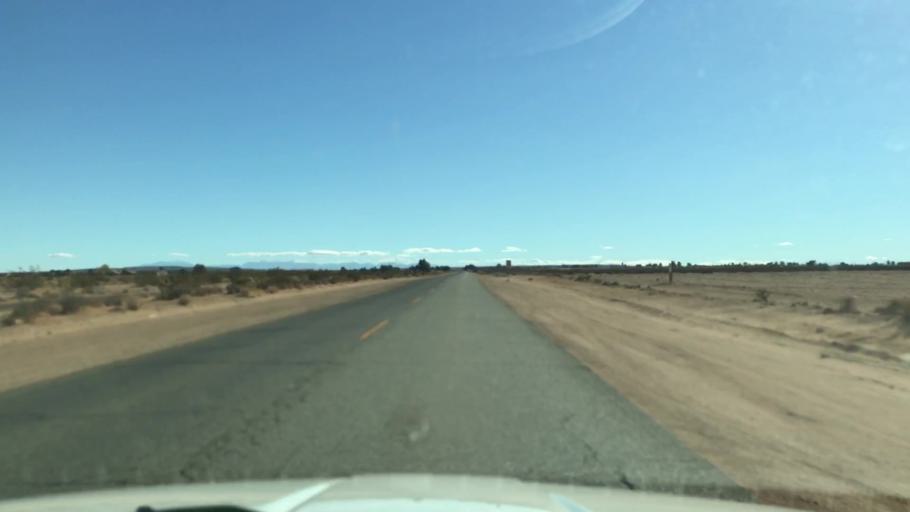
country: US
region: California
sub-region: Kern County
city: California City
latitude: 35.1475
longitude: -117.9859
